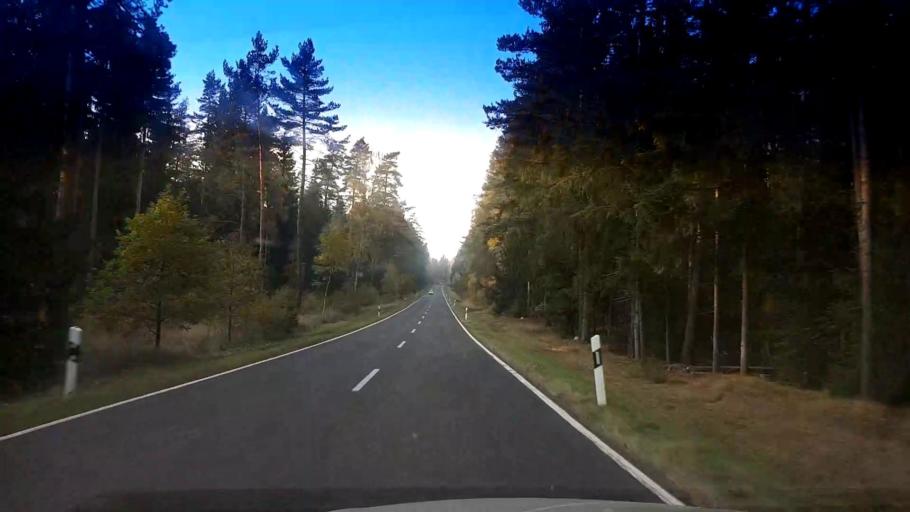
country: DE
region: Bavaria
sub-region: Upper Franconia
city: Schirnding
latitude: 50.0679
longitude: 12.2452
